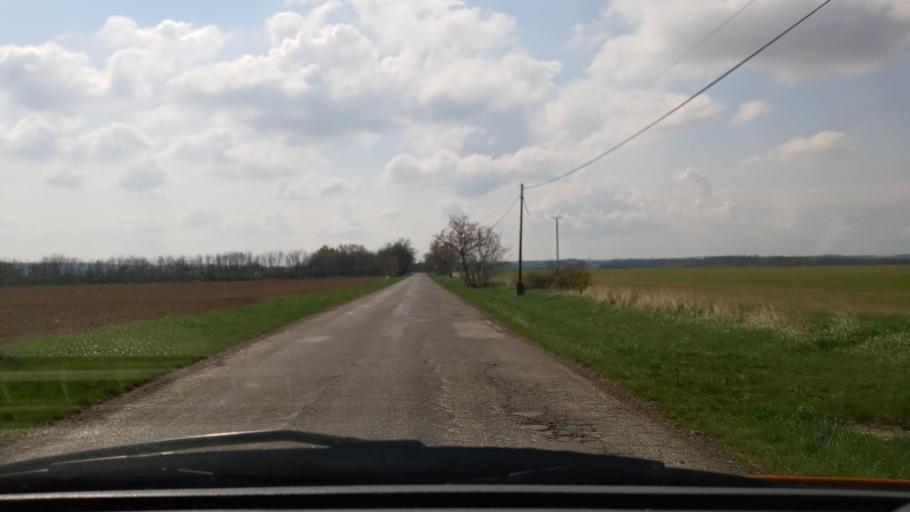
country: HU
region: Baranya
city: Pecsvarad
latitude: 46.0868
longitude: 18.5048
